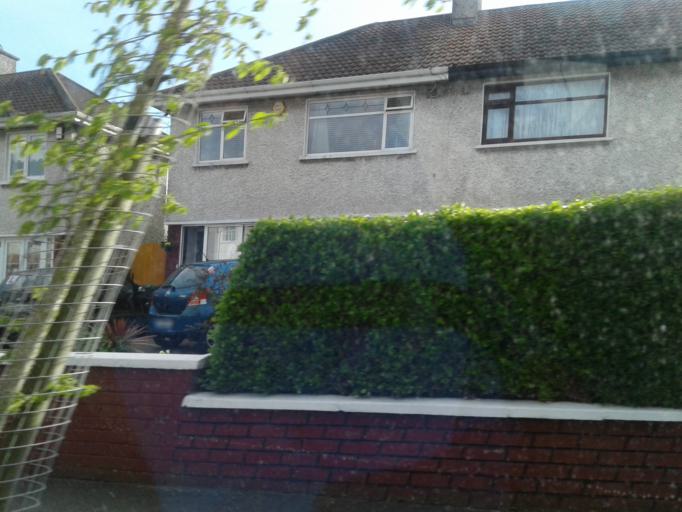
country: IE
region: Leinster
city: Artane
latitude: 53.3811
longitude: -6.2238
